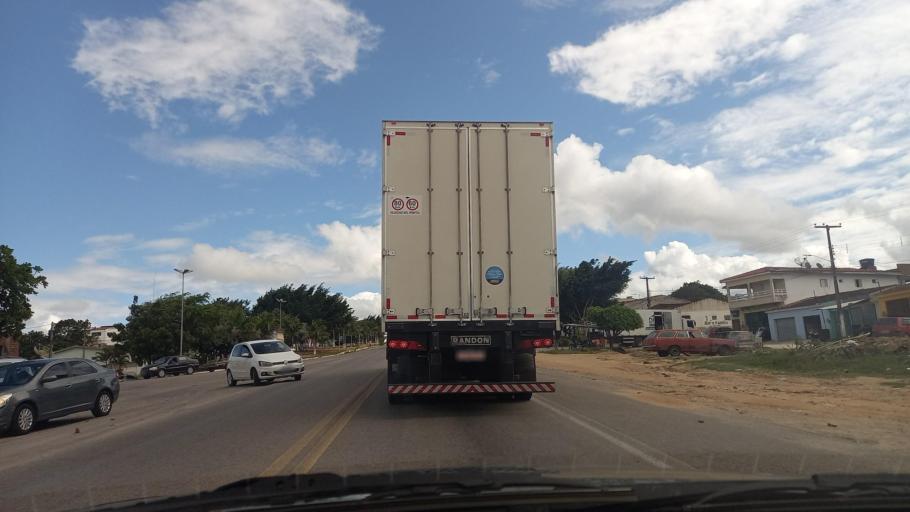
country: BR
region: Pernambuco
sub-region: Lajedo
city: Lajedo
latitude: -8.7104
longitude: -36.4195
